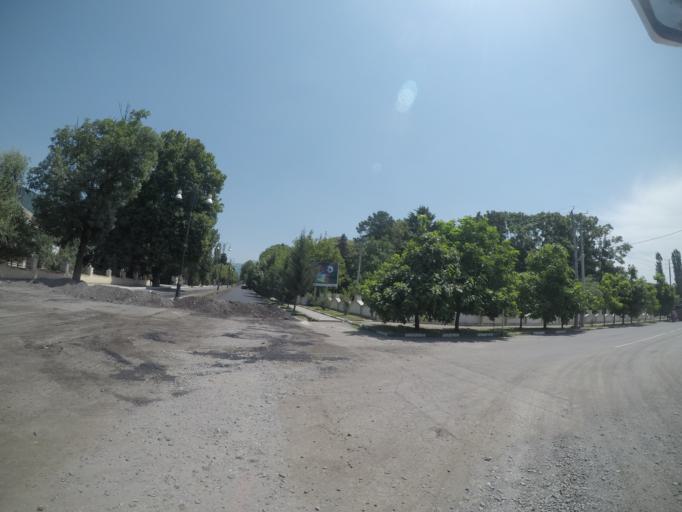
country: AZ
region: Qakh Rayon
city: Qax
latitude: 41.4168
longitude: 46.9063
